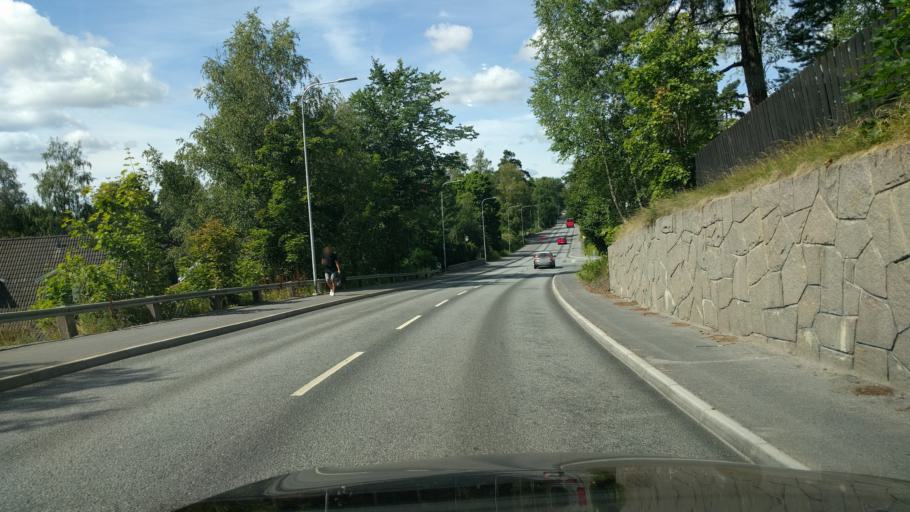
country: SE
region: Stockholm
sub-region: Taby Kommun
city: Taby
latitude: 59.4505
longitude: 18.0575
